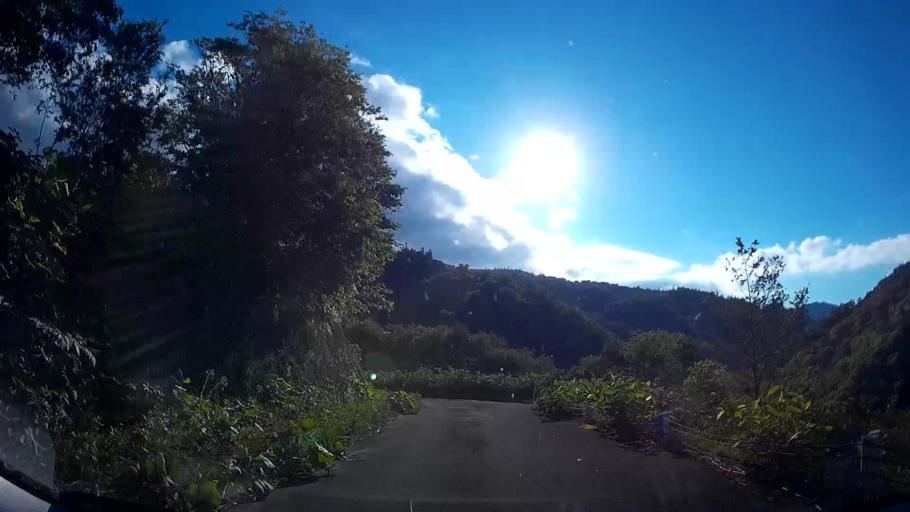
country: JP
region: Hokkaido
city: Otaru
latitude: 42.9807
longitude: 141.0432
